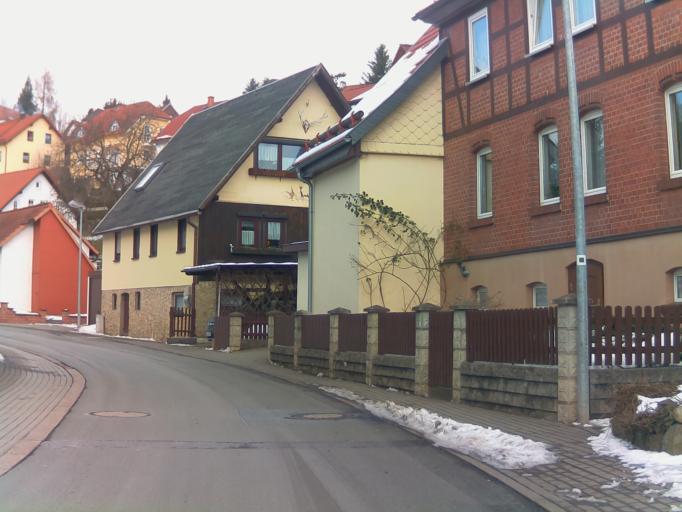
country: DE
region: Thuringia
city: Zella-Mehlis
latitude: 50.6181
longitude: 10.6387
